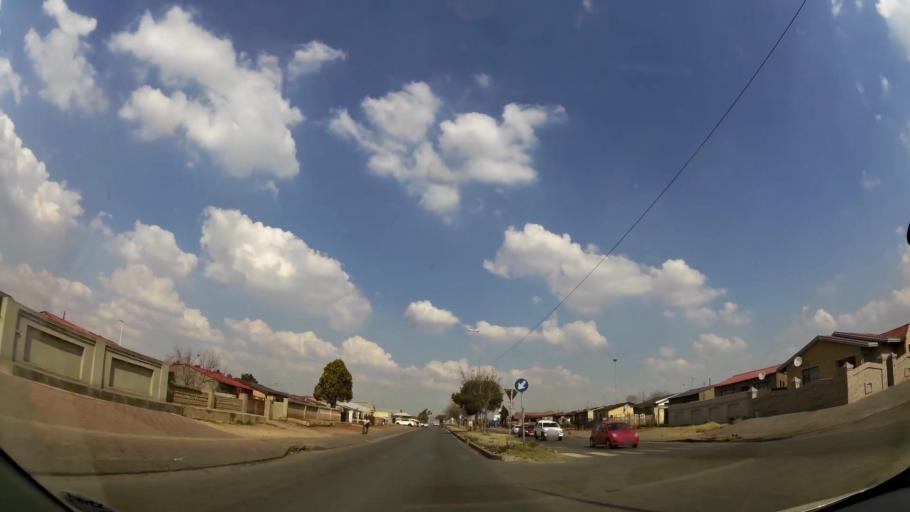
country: ZA
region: Gauteng
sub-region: Ekurhuleni Metropolitan Municipality
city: Germiston
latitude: -26.3420
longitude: 28.1619
